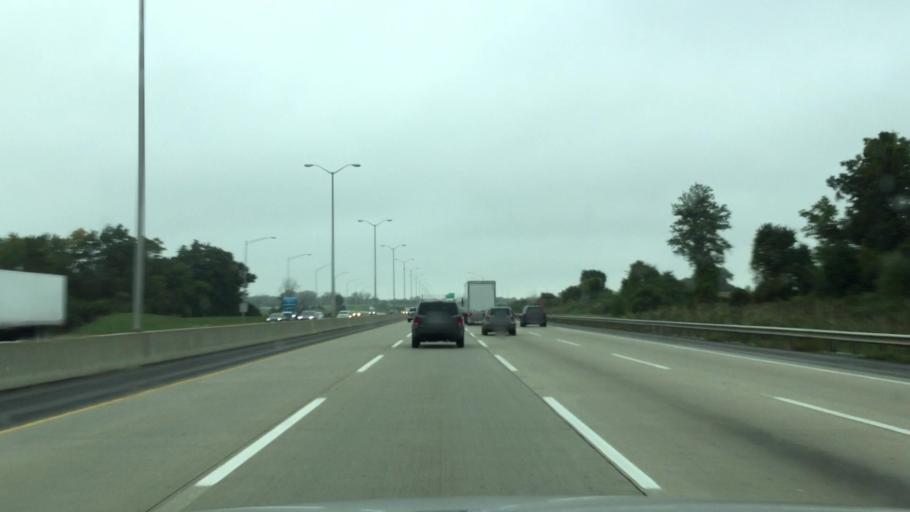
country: US
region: Illinois
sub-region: Lake County
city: Wadsworth
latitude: 42.4576
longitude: -87.9612
